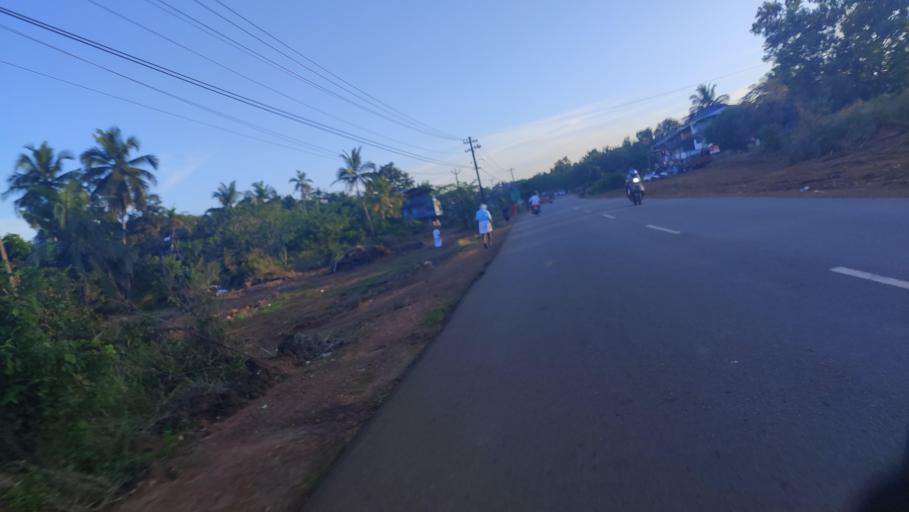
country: IN
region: Kerala
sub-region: Kasaragod District
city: Kannangad
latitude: 12.4057
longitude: 75.0966
